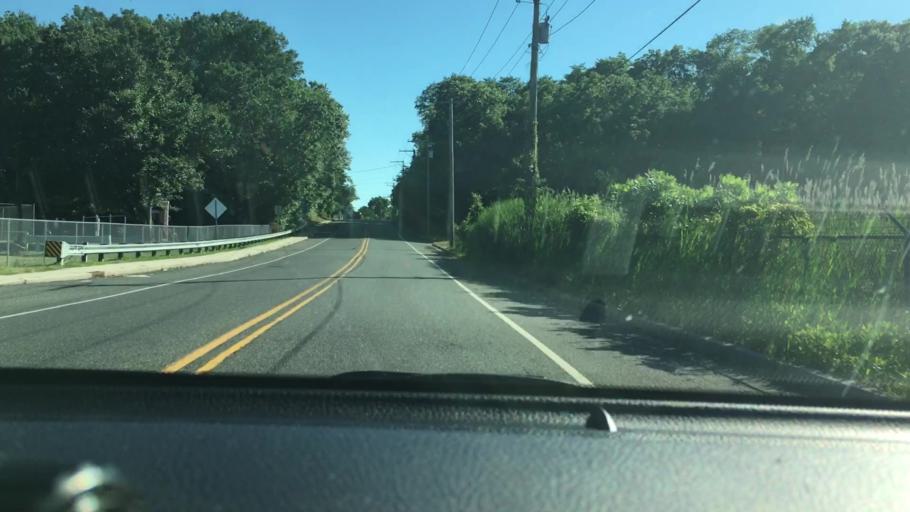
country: US
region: New Jersey
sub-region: Cumberland County
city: Millville
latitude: 39.3999
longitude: -75.0542
